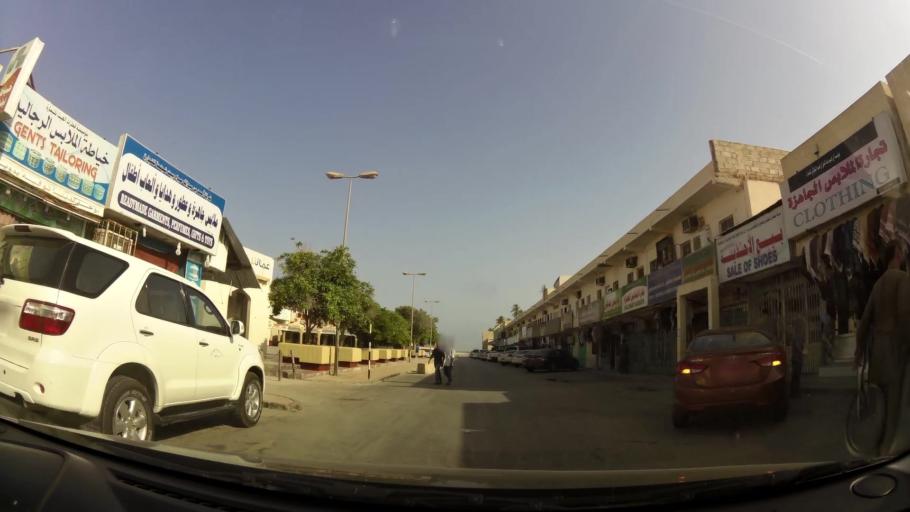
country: OM
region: Zufar
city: Salalah
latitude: 17.0019
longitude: 54.1010
